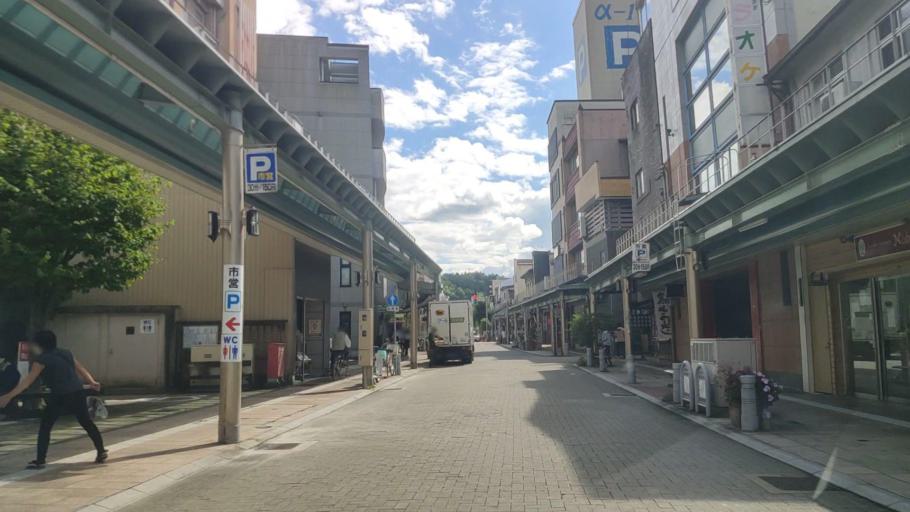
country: JP
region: Gifu
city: Takayama
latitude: 36.1438
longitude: 137.2573
